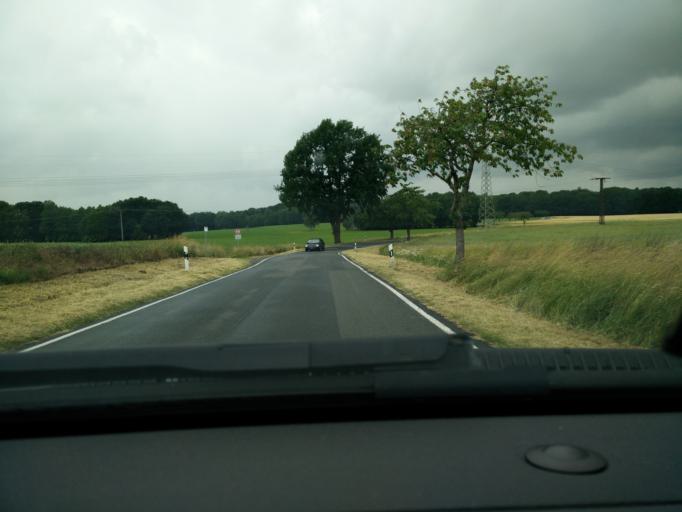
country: DE
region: Saxony
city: Bad Lausick
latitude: 51.1433
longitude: 12.6872
